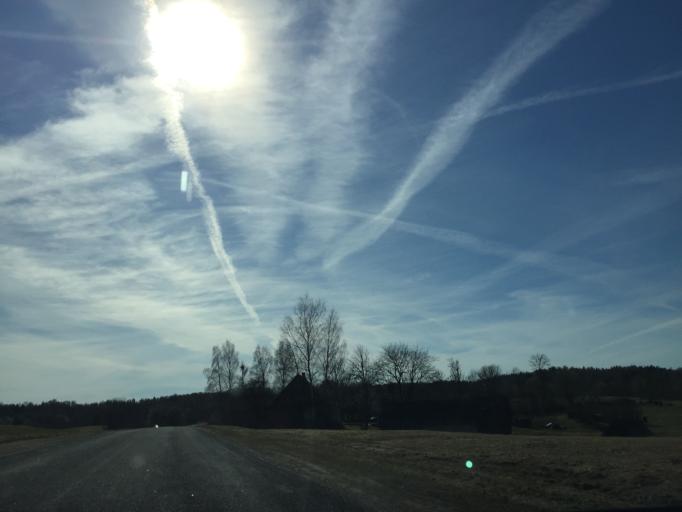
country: EE
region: Vorumaa
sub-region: Antsla vald
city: Vana-Antsla
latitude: 57.9942
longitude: 26.4188
